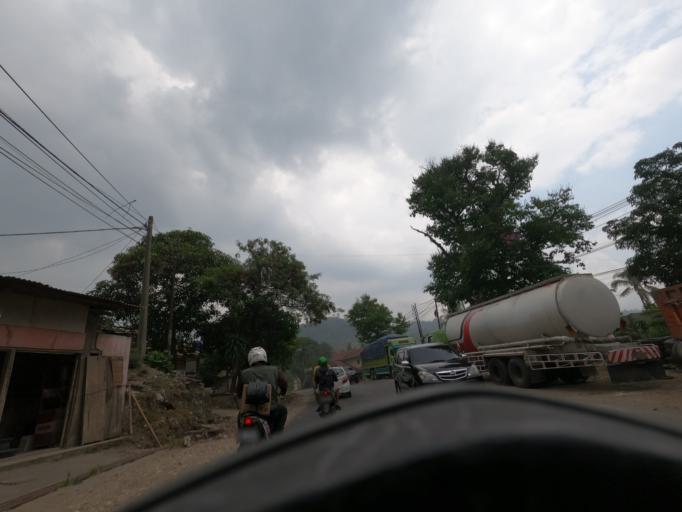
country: ID
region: West Java
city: Padalarang
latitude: -6.8315
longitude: 107.4534
